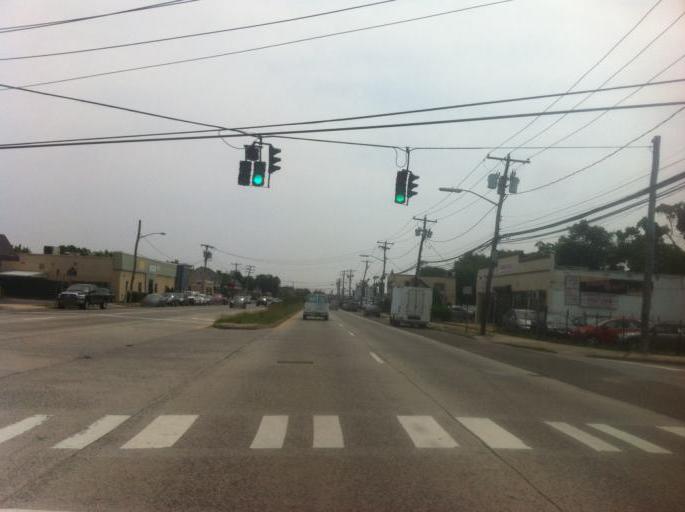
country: US
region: New York
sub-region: Nassau County
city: Hicksville
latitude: 40.7592
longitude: -73.5136
